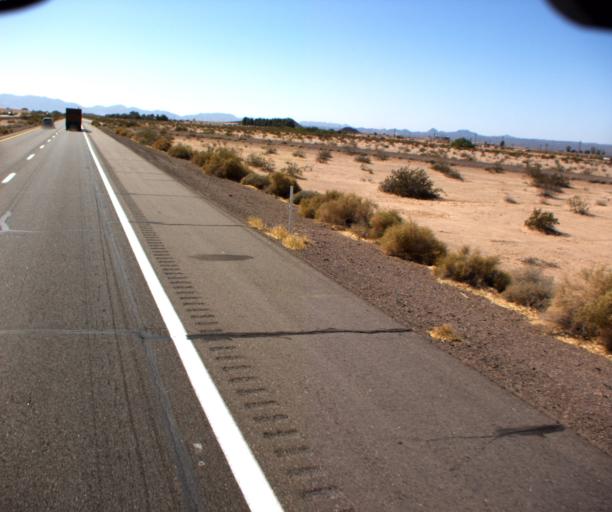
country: US
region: Arizona
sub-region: Yuma County
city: Wellton
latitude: 32.6815
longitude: -114.0230
